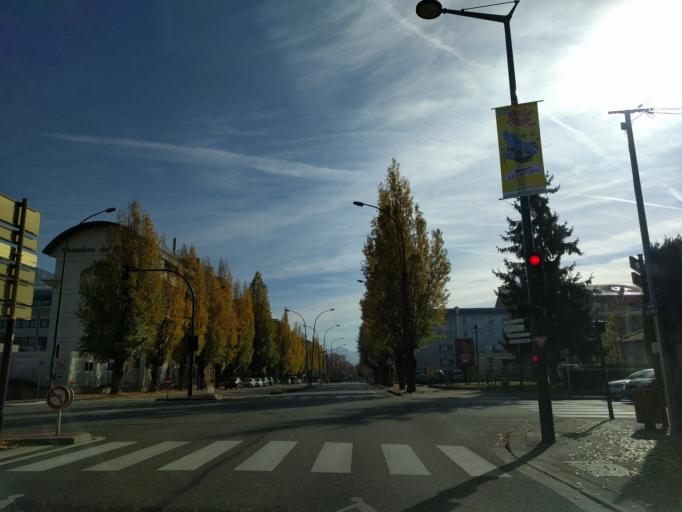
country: FR
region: Rhone-Alpes
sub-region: Departement de la Haute-Savoie
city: Annecy-le-Vieux
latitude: 45.9105
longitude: 6.1376
